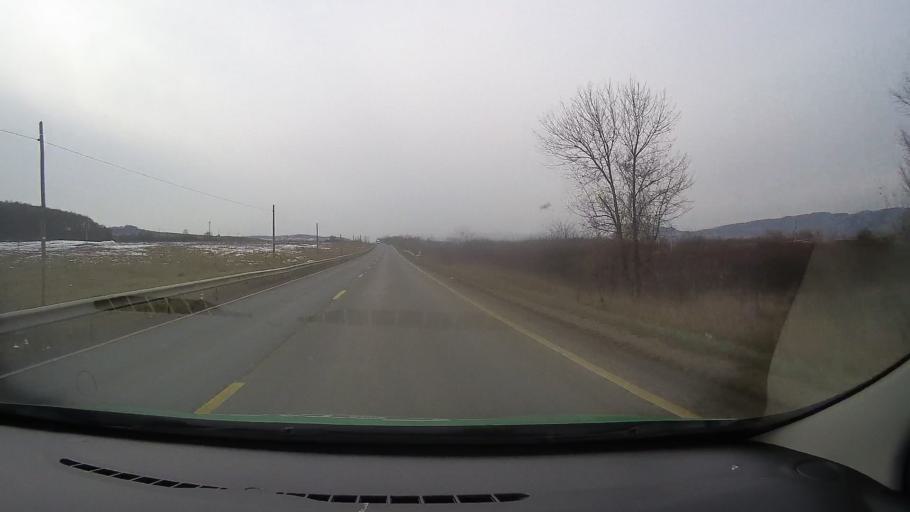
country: RO
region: Hunedoara
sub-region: Comuna Turdas
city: Turdas
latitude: 45.8352
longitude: 23.1052
